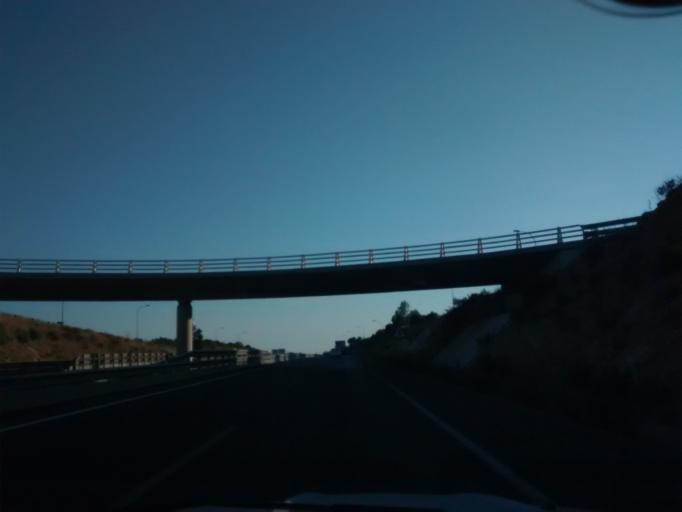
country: ES
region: Balearic Islands
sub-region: Illes Balears
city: Inca
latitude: 39.7348
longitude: 2.9391
